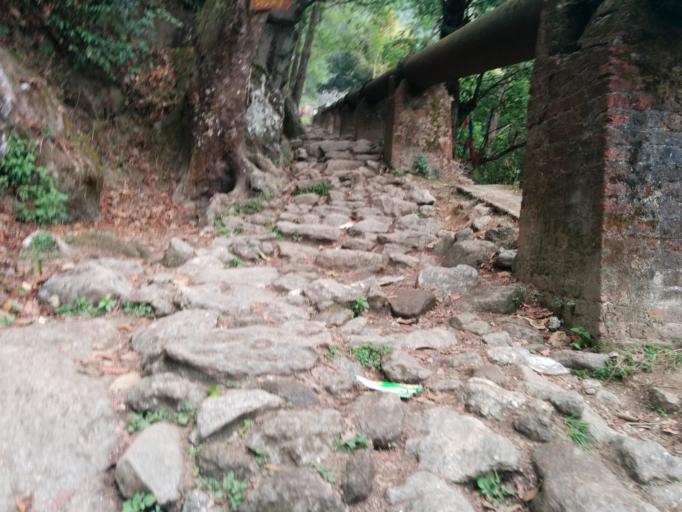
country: NP
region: Central Region
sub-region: Bagmati Zone
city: Bhaktapur
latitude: 27.7663
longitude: 85.4237
